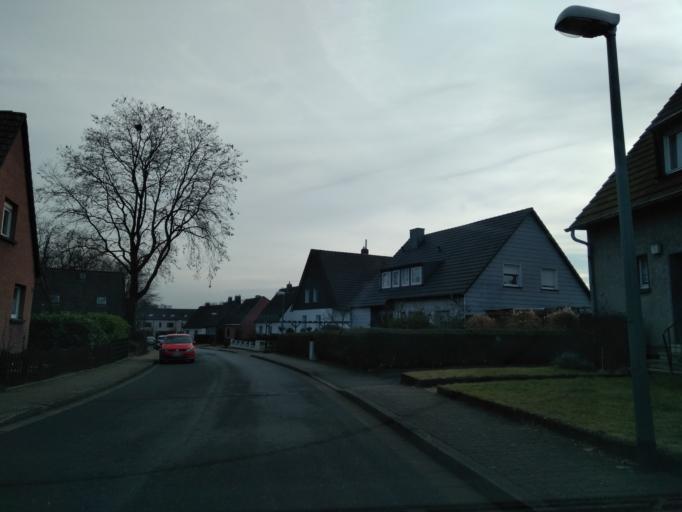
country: DE
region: North Rhine-Westphalia
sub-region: Regierungsbezirk Munster
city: Gladbeck
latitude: 51.5847
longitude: 7.0210
